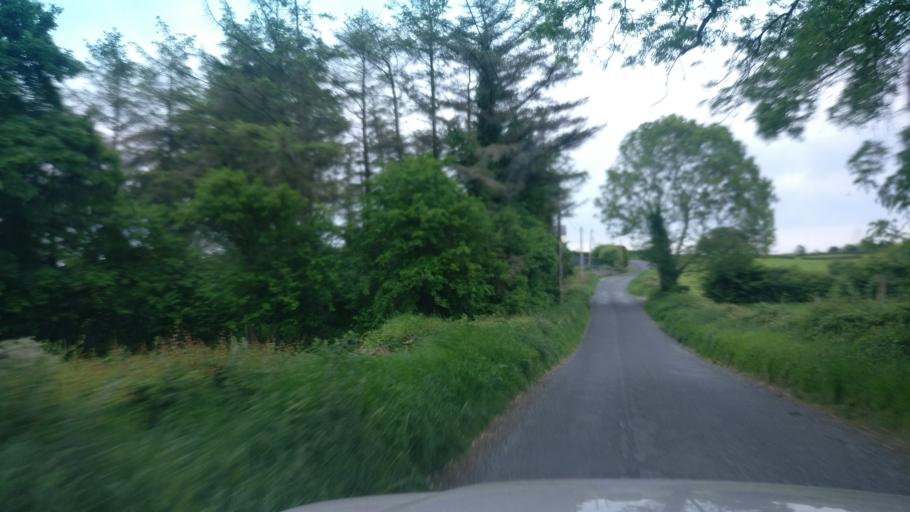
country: IE
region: Connaught
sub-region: County Galway
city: Portumna
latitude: 53.1485
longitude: -8.2912
